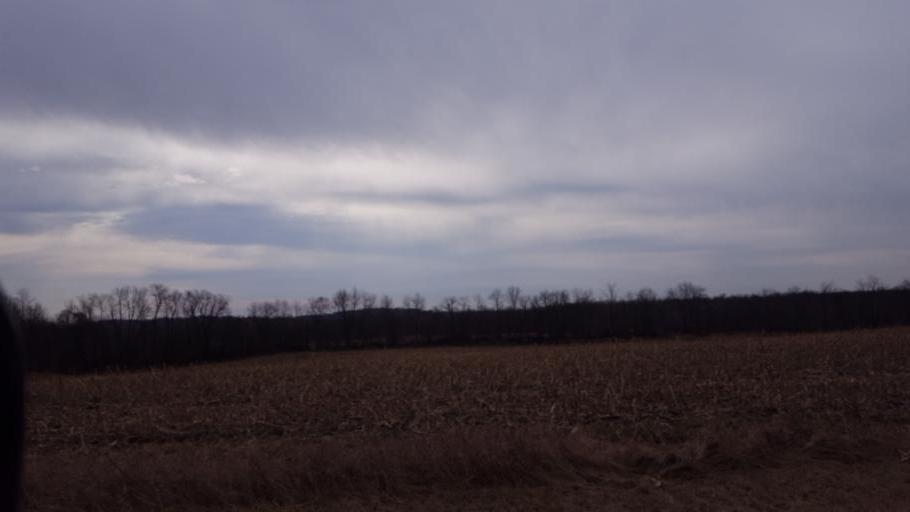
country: US
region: Ohio
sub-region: Richland County
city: Mansfield
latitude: 40.8078
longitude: -82.5487
